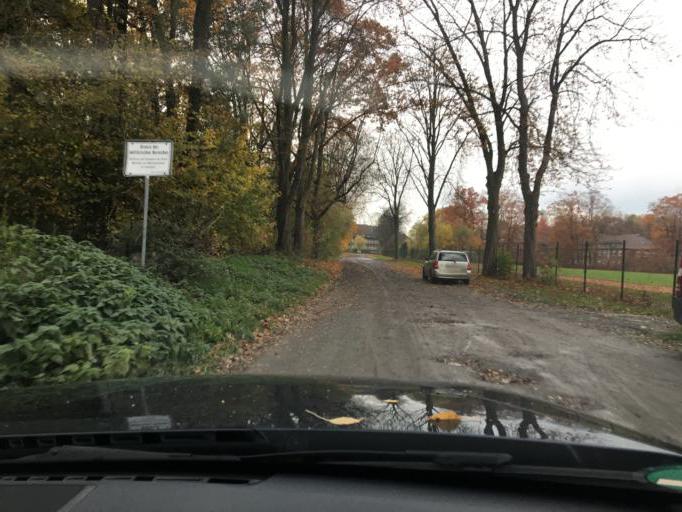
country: DE
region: North Rhine-Westphalia
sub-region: Regierungsbezirk Munster
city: Telgte
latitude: 51.9978
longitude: 7.7242
